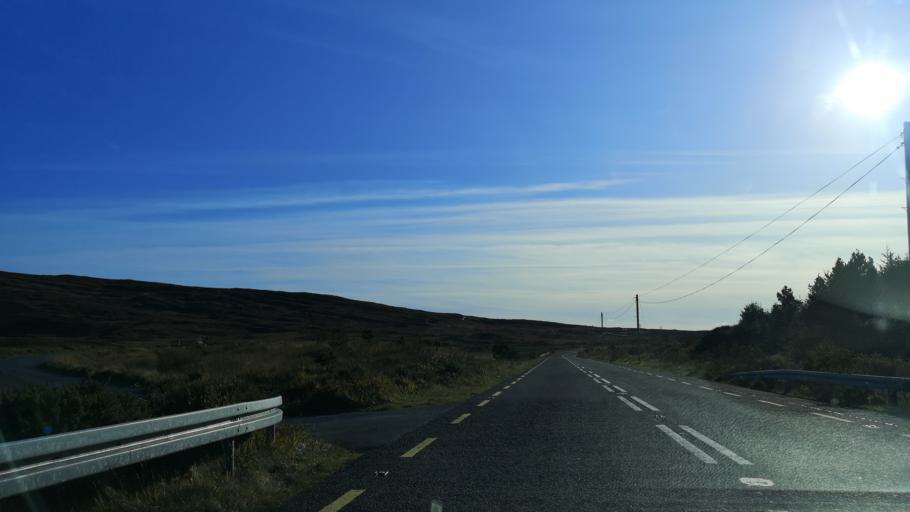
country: IE
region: Connaught
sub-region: County Galway
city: Clifden
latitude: 53.5341
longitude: -10.0380
